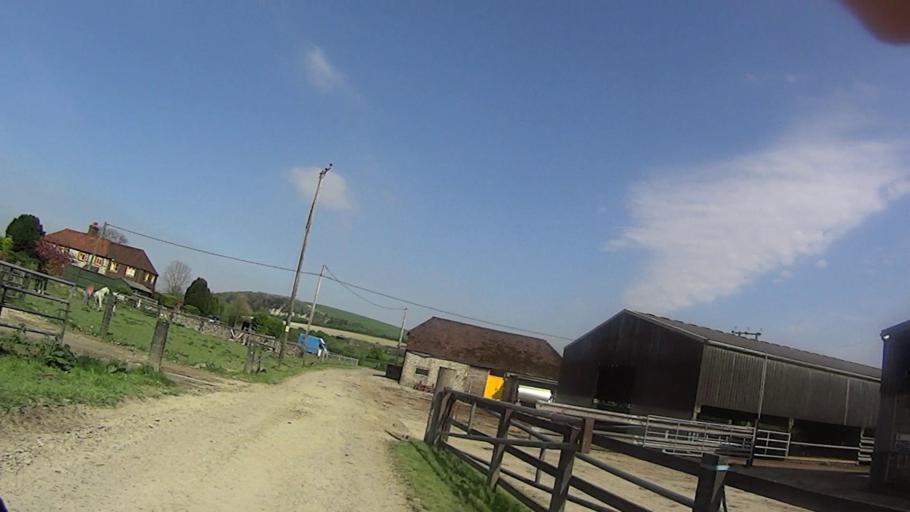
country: GB
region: England
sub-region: West Sussex
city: Midhurst
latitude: 50.9432
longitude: -0.7592
